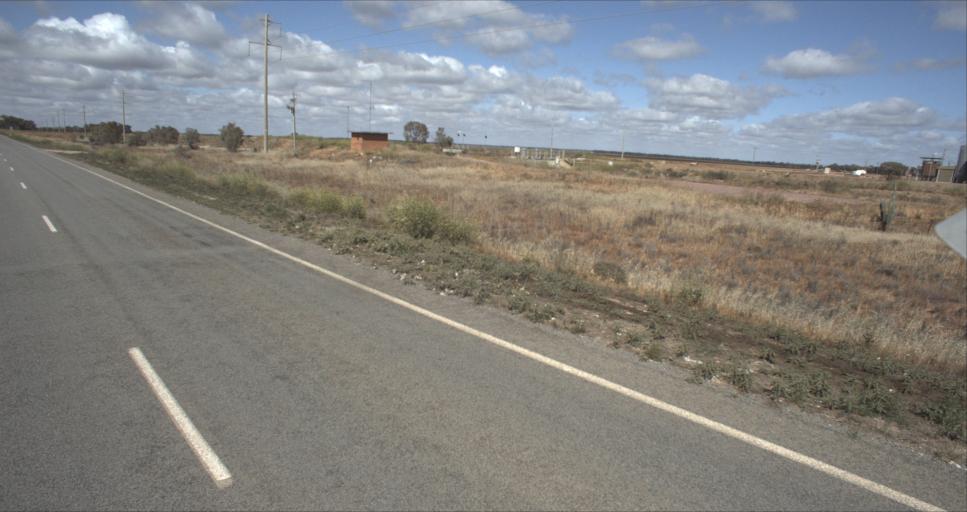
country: AU
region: New South Wales
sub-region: Murrumbidgee Shire
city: Darlington Point
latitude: -34.5480
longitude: 146.1710
